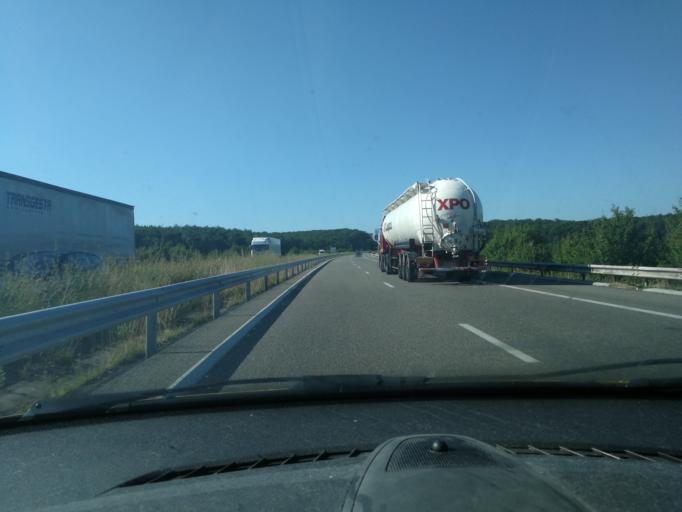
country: FR
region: Alsace
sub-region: Departement du Bas-Rhin
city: Sarrewerden
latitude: 48.8936
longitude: 7.1250
